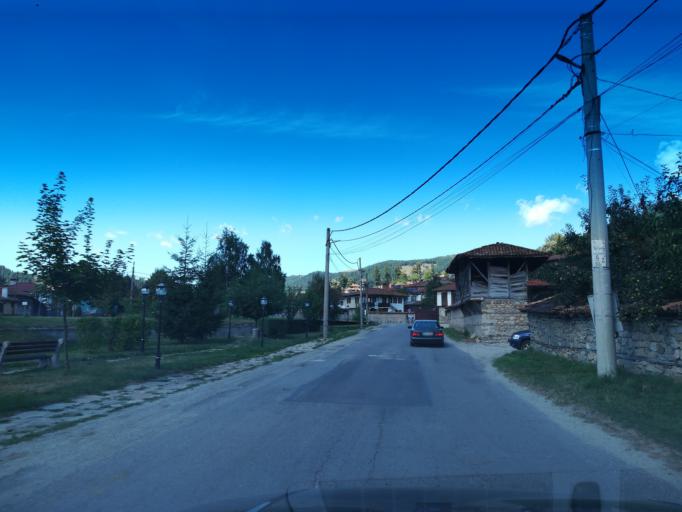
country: BG
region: Sofiya
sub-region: Obshtina Koprivshtitsa
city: Koprivshtitsa
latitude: 42.6340
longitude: 24.3618
